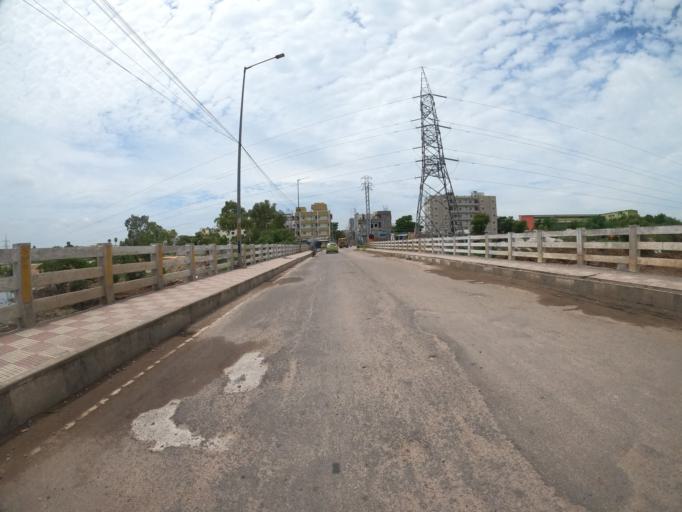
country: IN
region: Telangana
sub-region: Hyderabad
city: Hyderabad
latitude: 17.3711
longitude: 78.4122
